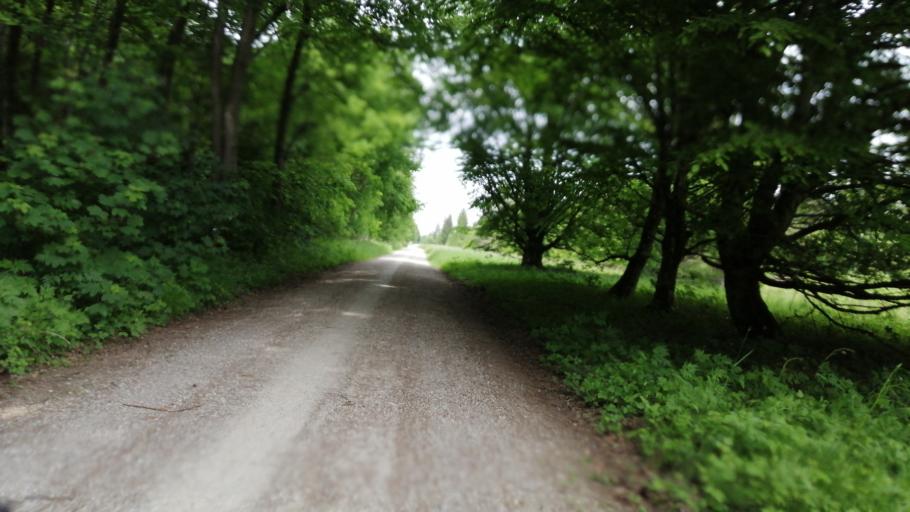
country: DE
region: Bavaria
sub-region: Upper Bavaria
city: Oberhaching
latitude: 48.0530
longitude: 11.5666
